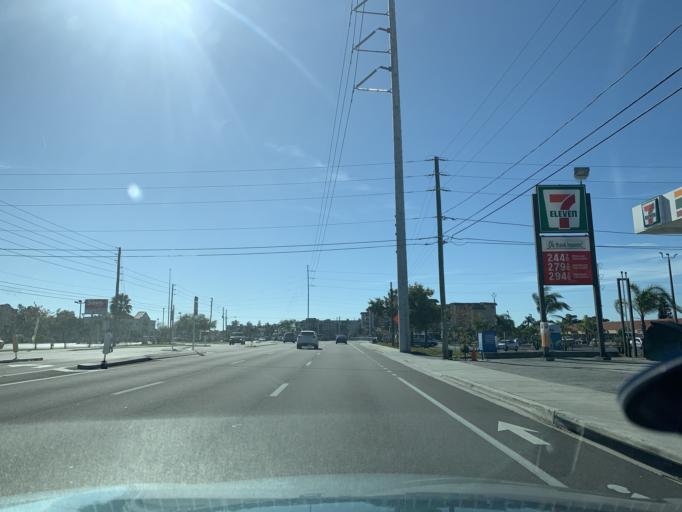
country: US
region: Florida
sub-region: Pinellas County
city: Seminole
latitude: 27.8416
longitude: -82.7625
